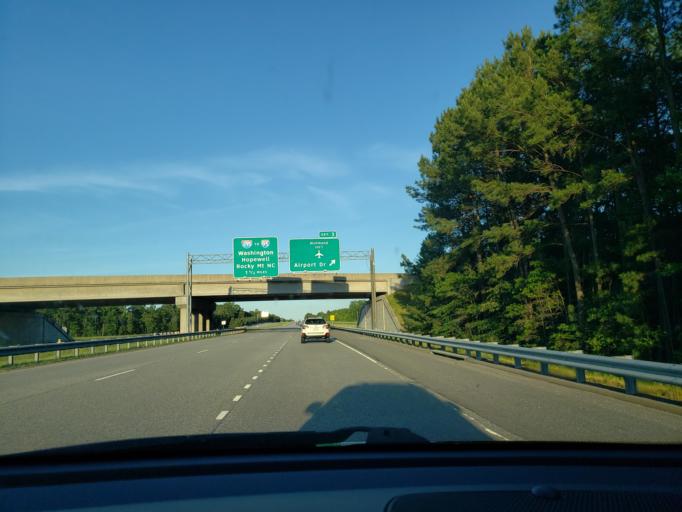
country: US
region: Virginia
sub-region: Henrico County
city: Fort Lee
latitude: 37.4789
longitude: -77.3410
